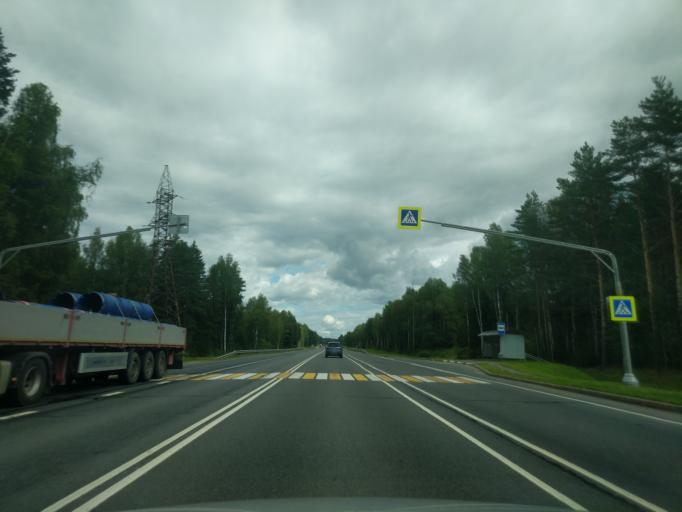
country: RU
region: Jaroslavl
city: Nekrasovskoye
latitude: 57.5875
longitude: 40.2948
